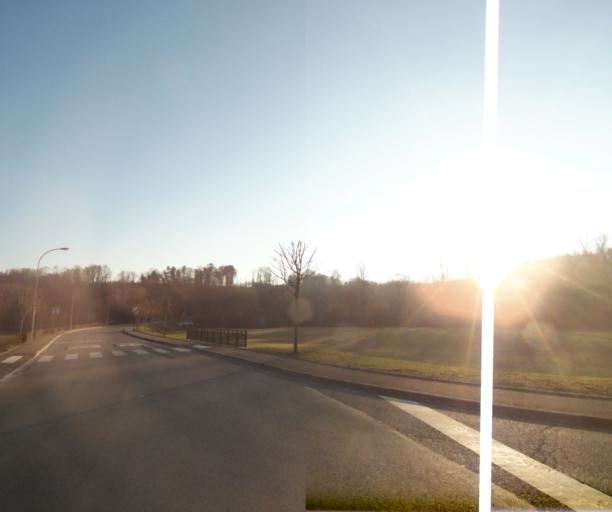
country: FR
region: Champagne-Ardenne
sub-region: Departement de la Haute-Marne
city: Bienville
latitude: 48.5500
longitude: 5.0744
